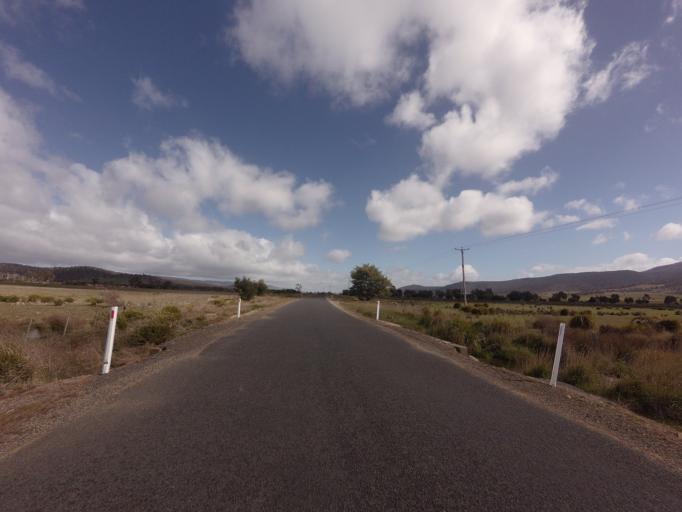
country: AU
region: Tasmania
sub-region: Break O'Day
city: St Helens
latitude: -41.8248
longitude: 147.8489
